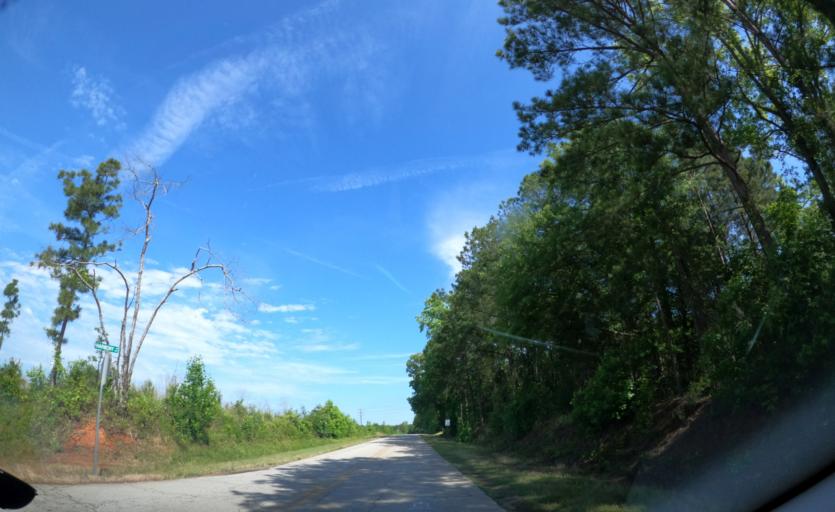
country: US
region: Georgia
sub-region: Elbert County
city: Elberton
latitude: 34.1590
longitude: -82.8321
